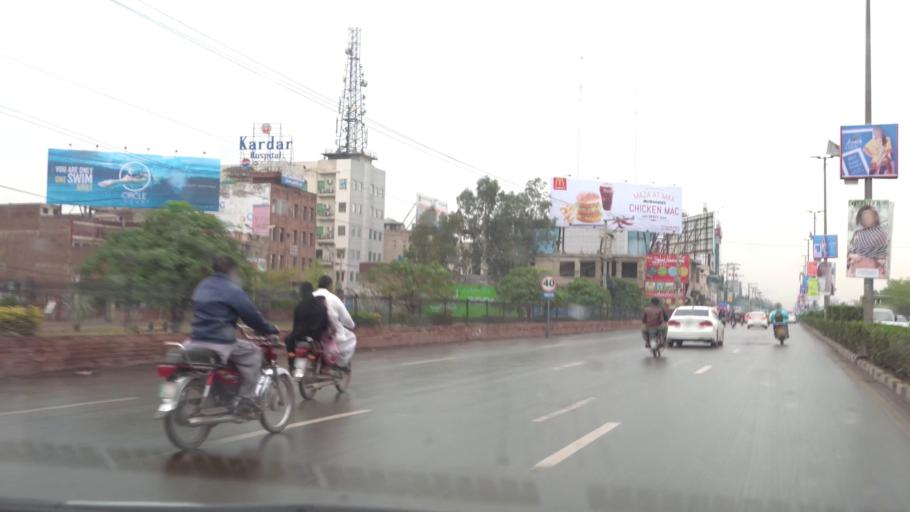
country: PK
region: Punjab
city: Faisalabad
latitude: 31.4180
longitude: 73.1069
